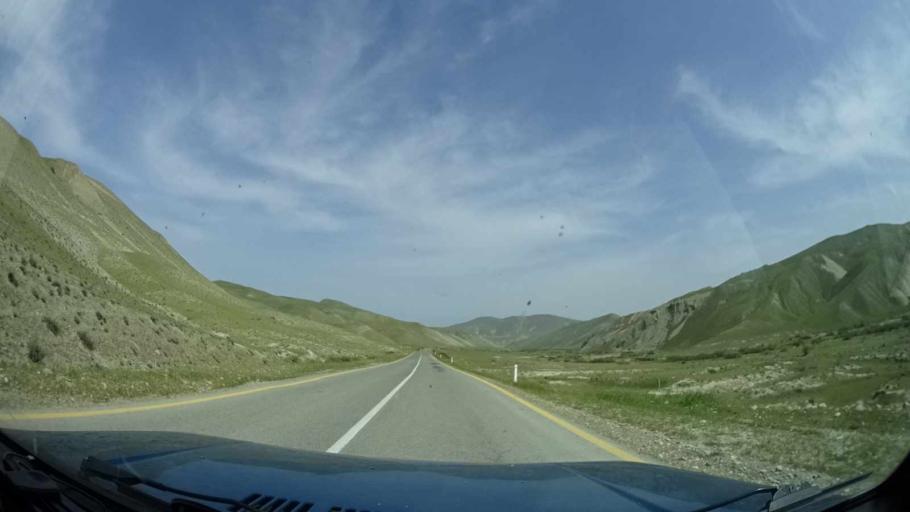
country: AZ
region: Xizi
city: Kilyazi
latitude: 40.8539
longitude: 49.2390
